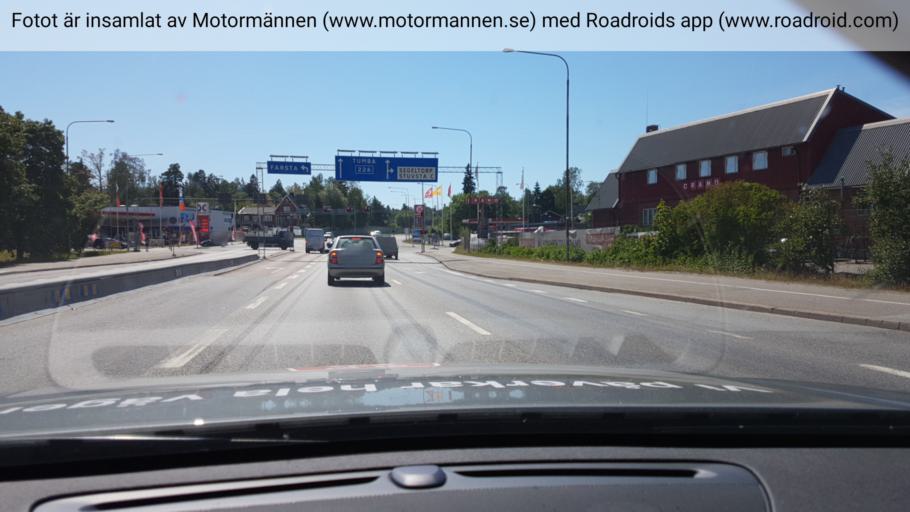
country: SE
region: Stockholm
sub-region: Huddinge Kommun
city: Huddinge
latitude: 59.2515
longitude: 18.0099
